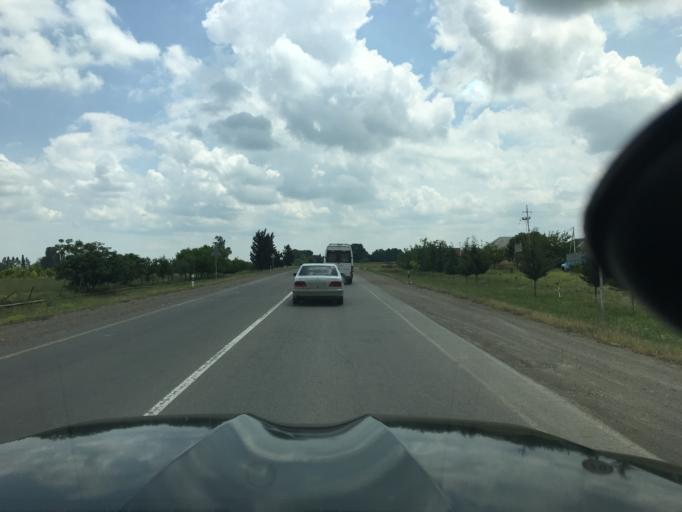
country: AZ
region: Tovuz
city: Tovuz
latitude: 40.9539
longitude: 45.7418
